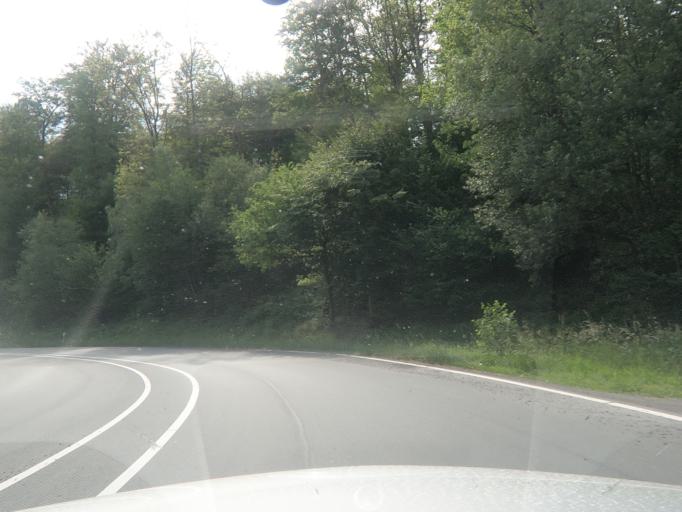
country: DE
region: North Rhine-Westphalia
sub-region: Regierungsbezirk Arnsberg
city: Olpe
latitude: 51.0440
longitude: 7.8682
